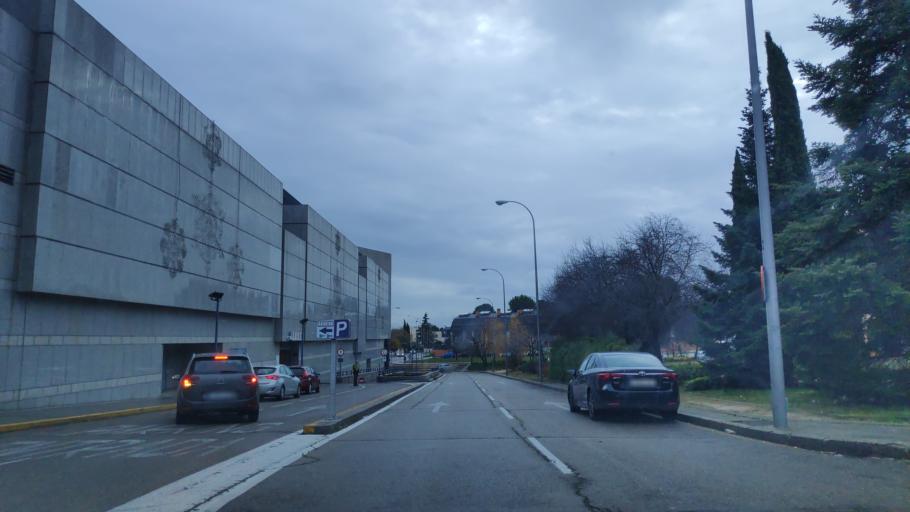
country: ES
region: Madrid
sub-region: Provincia de Madrid
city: San Blas
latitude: 40.4558
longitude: -3.6179
